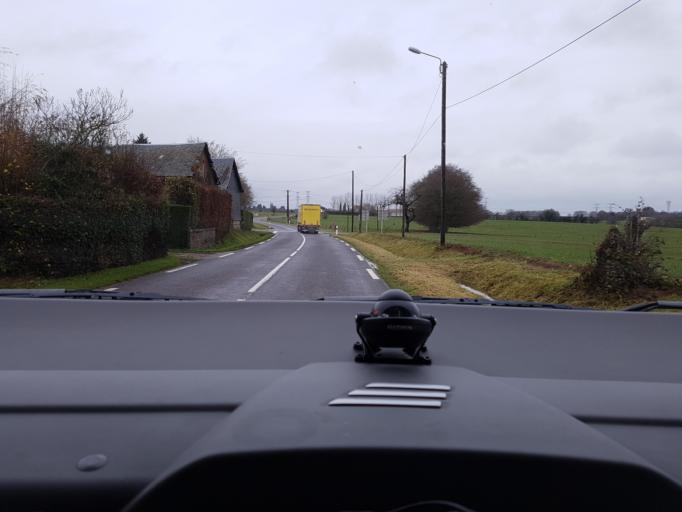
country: FR
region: Haute-Normandie
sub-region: Departement de la Seine-Maritime
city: Gournay-en-Bray
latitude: 49.4438
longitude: 1.6609
